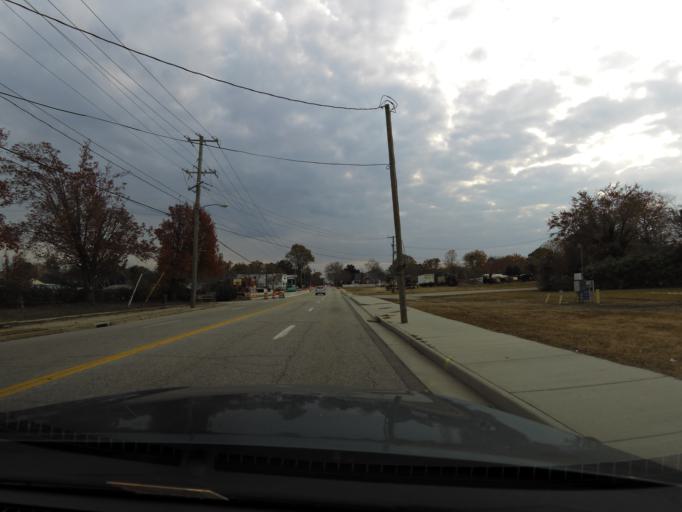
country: US
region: Virginia
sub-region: City of Hampton
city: Hampton
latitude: 37.0180
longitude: -76.3530
